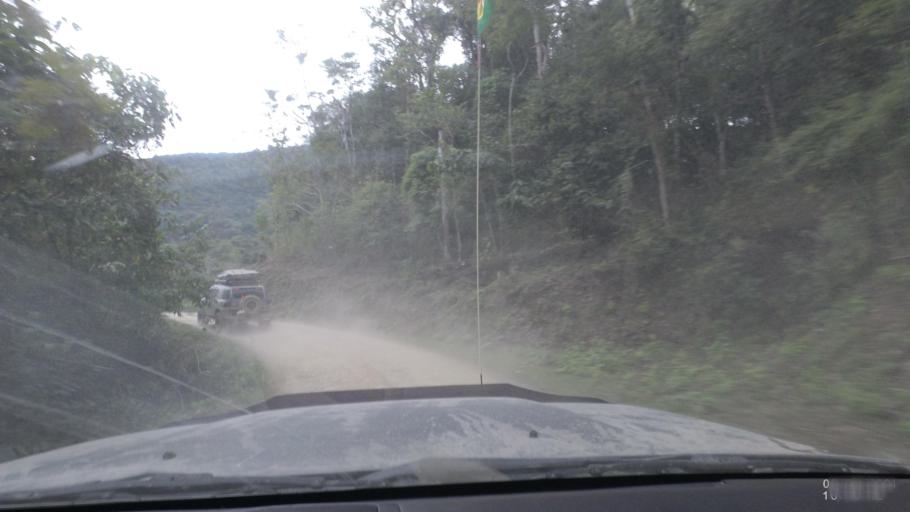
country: BO
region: La Paz
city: Quime
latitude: -16.5091
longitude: -66.7605
